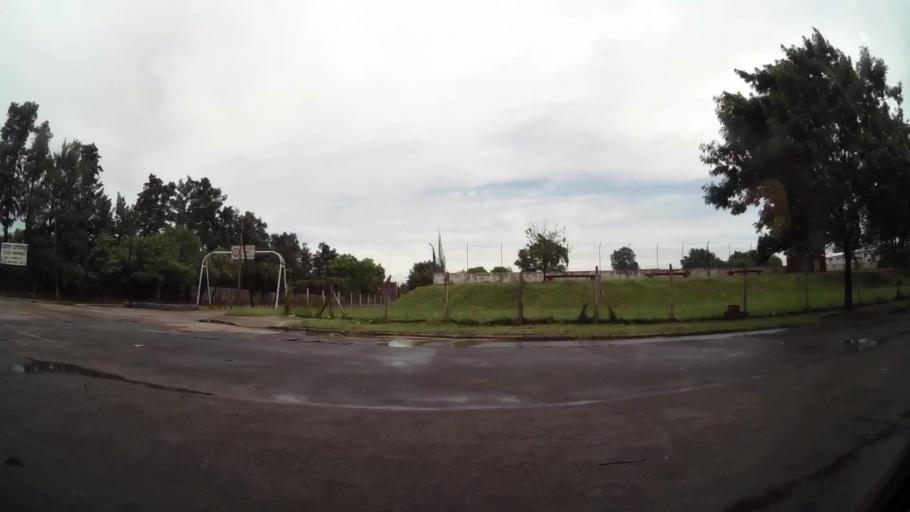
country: AR
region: Buenos Aires F.D.
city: Villa Lugano
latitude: -34.6545
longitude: -58.4493
